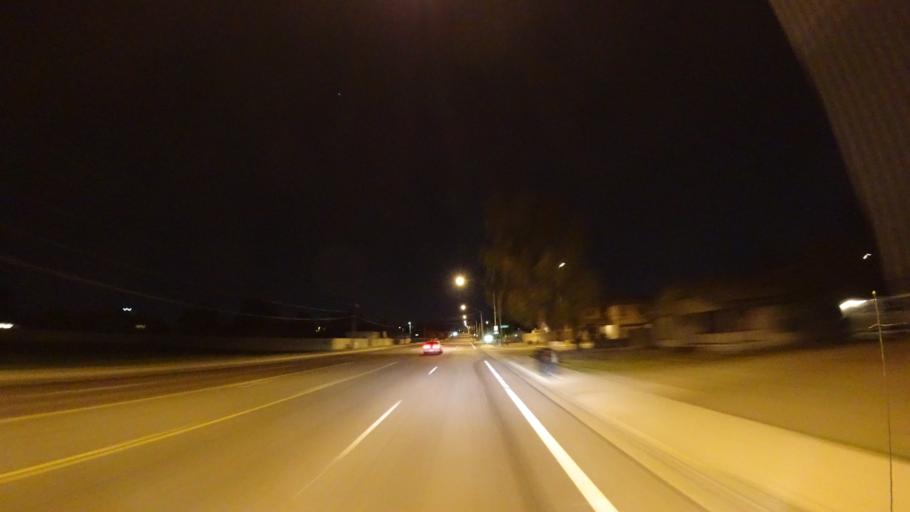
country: US
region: Arizona
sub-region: Maricopa County
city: Mesa
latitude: 33.4478
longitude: -111.8225
